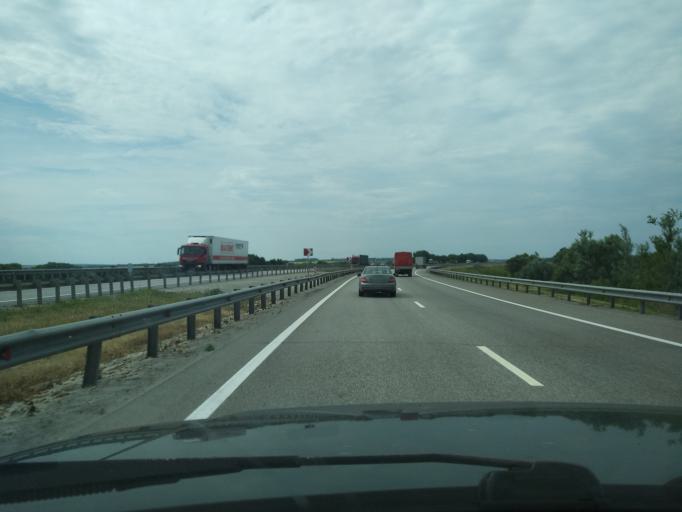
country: RU
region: Lipetsk
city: Khlevnoye
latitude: 52.0595
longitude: 39.1845
